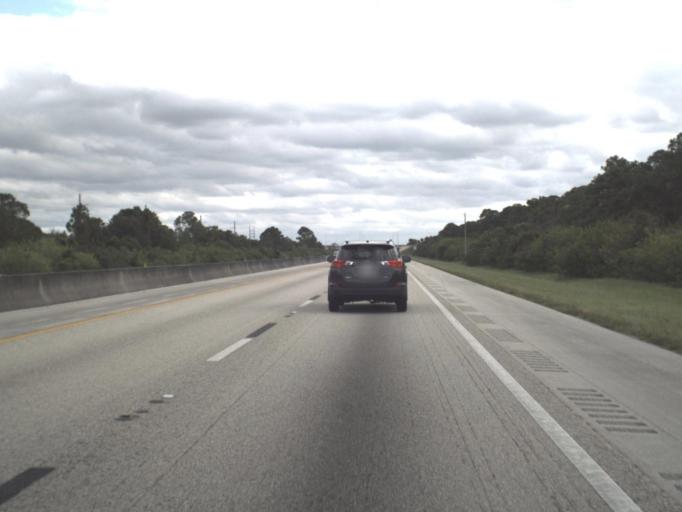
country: US
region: Florida
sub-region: Martin County
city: Palm City
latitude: 27.1327
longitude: -80.2853
